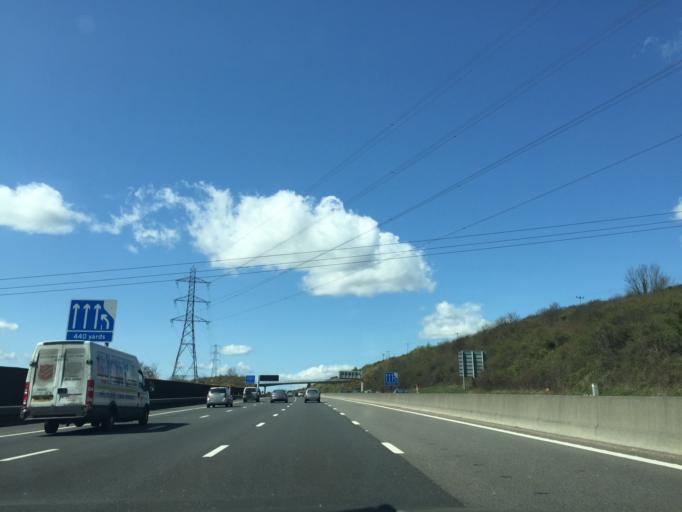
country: GB
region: England
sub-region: Portsmouth
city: Cosham
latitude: 50.8551
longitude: -1.1159
